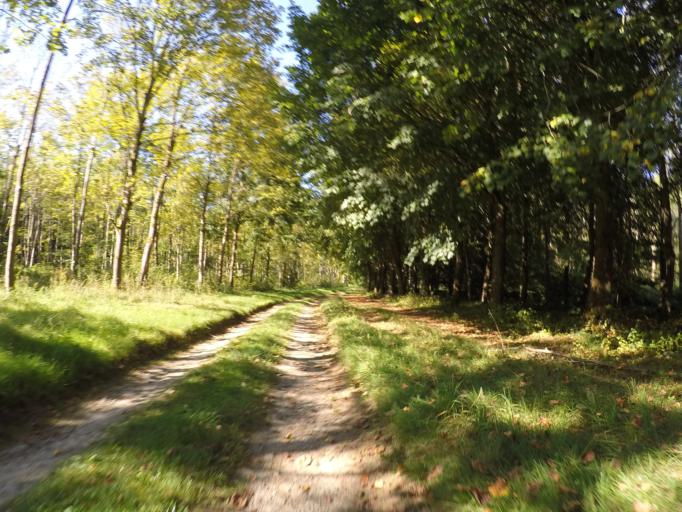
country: BE
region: Wallonia
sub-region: Province de Namur
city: Assesse
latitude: 50.3145
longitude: 5.0116
